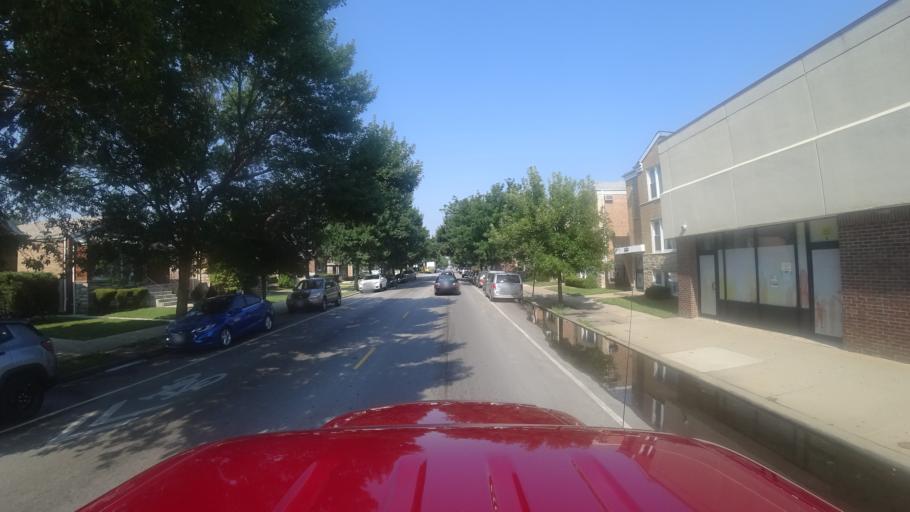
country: US
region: Illinois
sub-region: Cook County
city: Hometown
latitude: 41.7860
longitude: -87.7243
